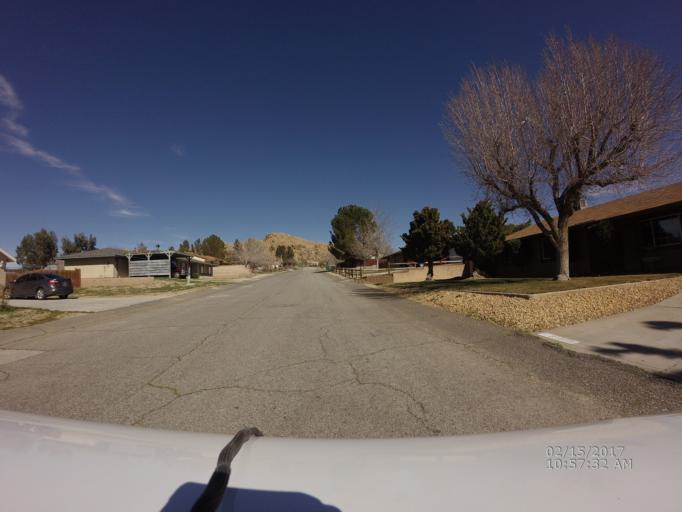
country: US
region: California
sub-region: Los Angeles County
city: Lake Los Angeles
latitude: 34.5848
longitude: -117.8517
